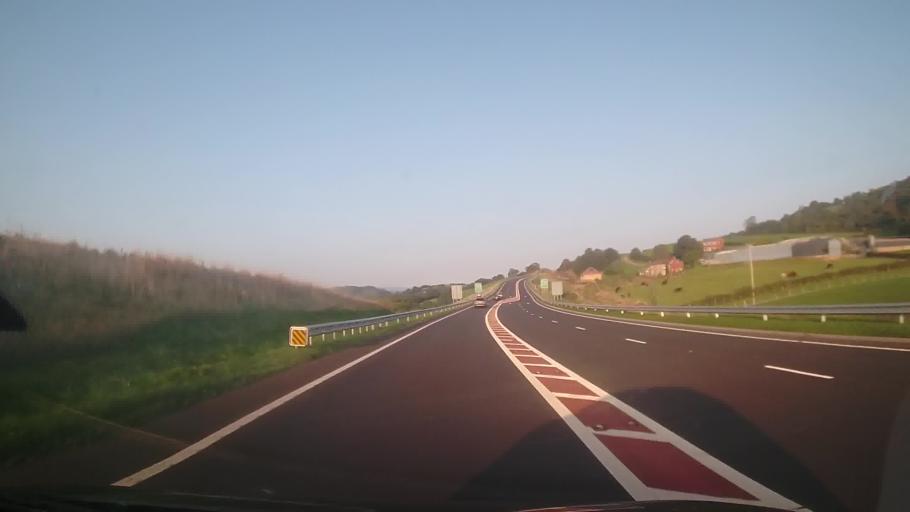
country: GB
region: Wales
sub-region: Sir Powys
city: Newtown
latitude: 52.5075
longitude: -3.3095
